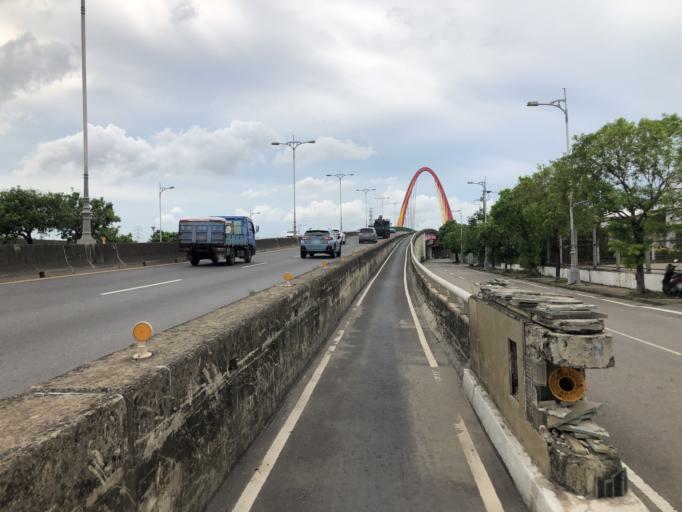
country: TW
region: Taiwan
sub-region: Changhua
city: Chang-hua
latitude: 24.0965
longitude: 120.6279
